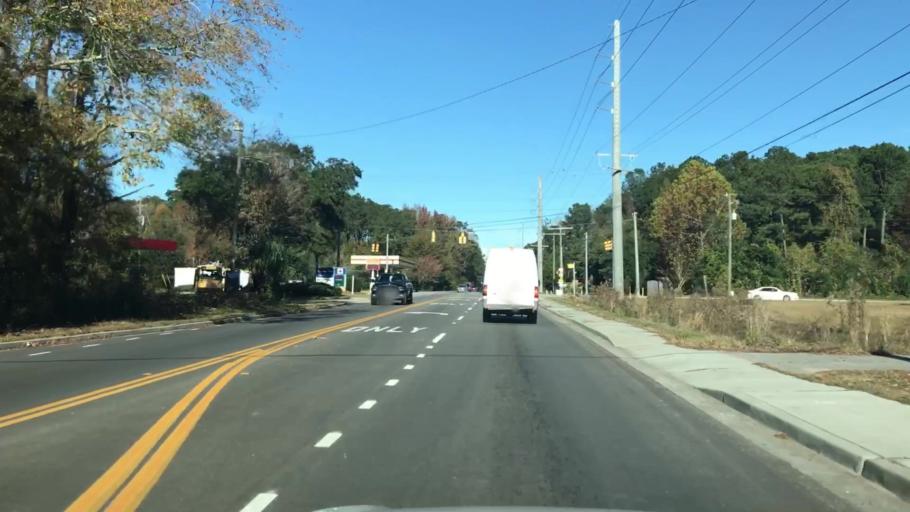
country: US
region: South Carolina
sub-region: Dorchester County
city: Summerville
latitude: 32.9957
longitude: -80.2276
